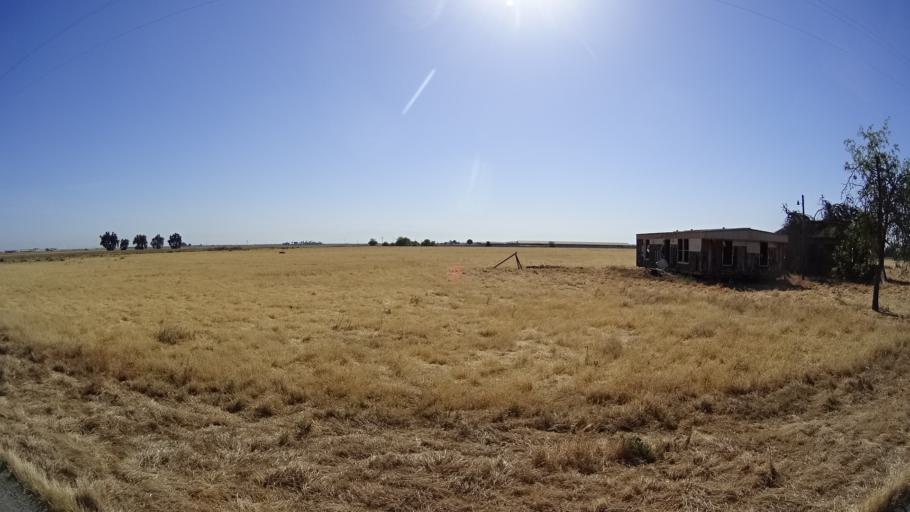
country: US
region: California
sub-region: Kings County
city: Home Garden
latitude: 36.2258
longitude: -119.5649
